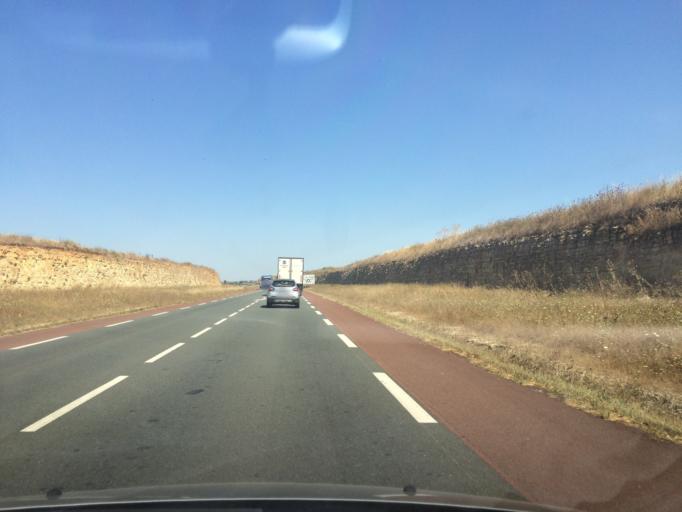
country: FR
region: Poitou-Charentes
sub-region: Departement de la Charente-Maritime
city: Esnandes
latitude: 46.2389
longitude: -1.0780
